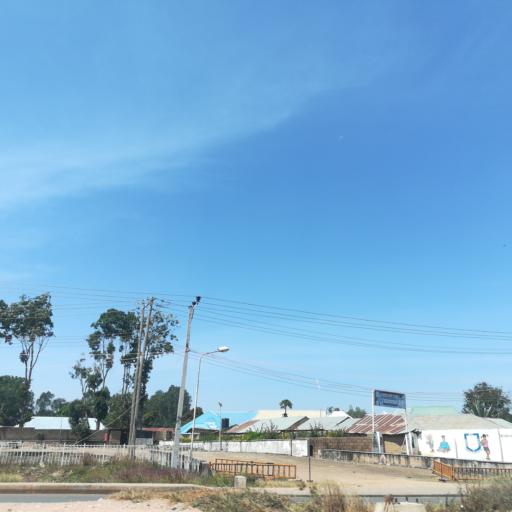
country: NG
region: Plateau
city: Bukuru
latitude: 9.7816
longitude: 8.8605
